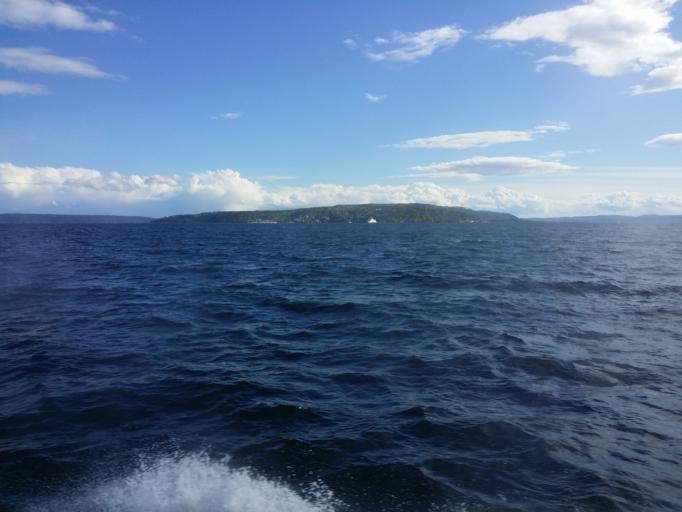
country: NO
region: Akershus
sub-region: Nesodden
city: Nesoddtangen
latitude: 59.8924
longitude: 10.6678
